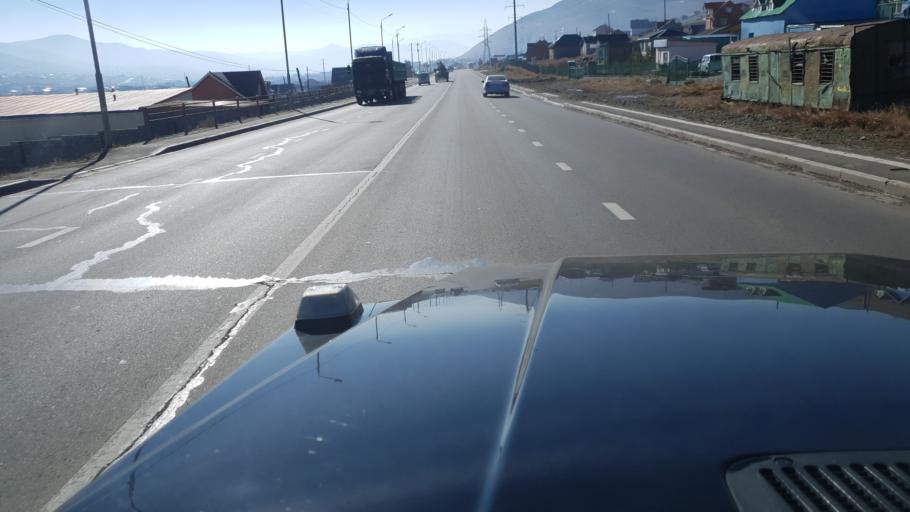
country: MN
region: Ulaanbaatar
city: Ulaanbaatar
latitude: 48.0271
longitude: 106.9124
